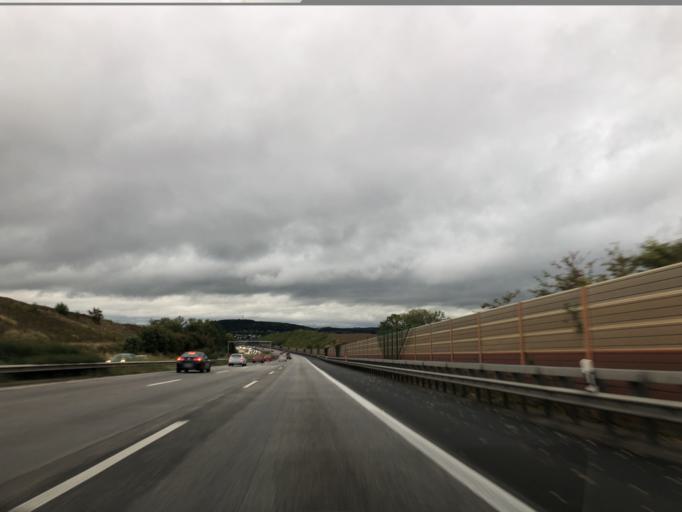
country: DE
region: Rheinland-Pfalz
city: Dernbach
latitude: 50.4459
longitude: 7.7993
